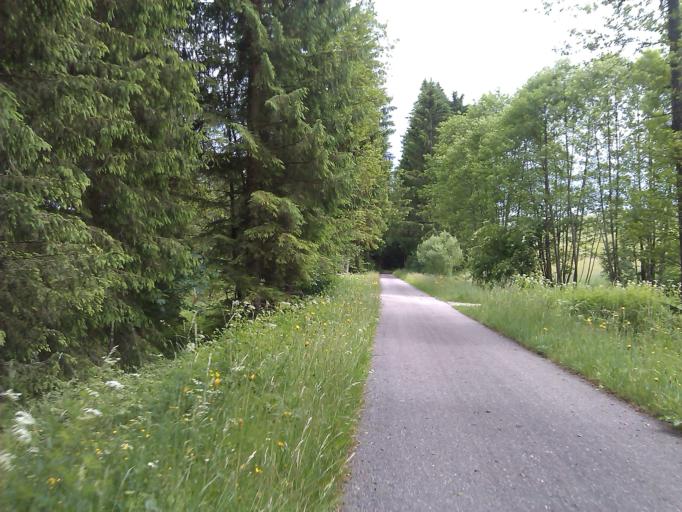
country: DE
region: Bavaria
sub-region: Swabia
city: Rosshaupten
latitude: 47.6911
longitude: 10.7046
